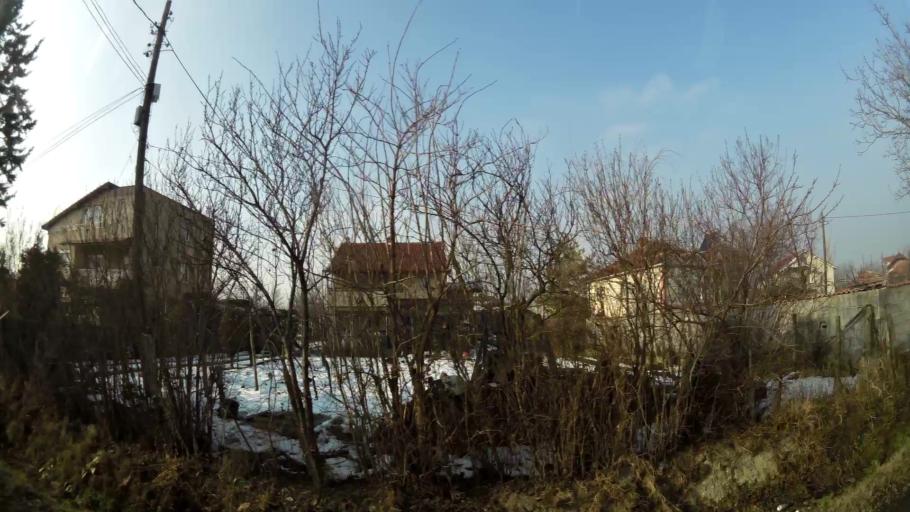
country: MK
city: Kadino
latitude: 41.9652
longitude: 21.5996
